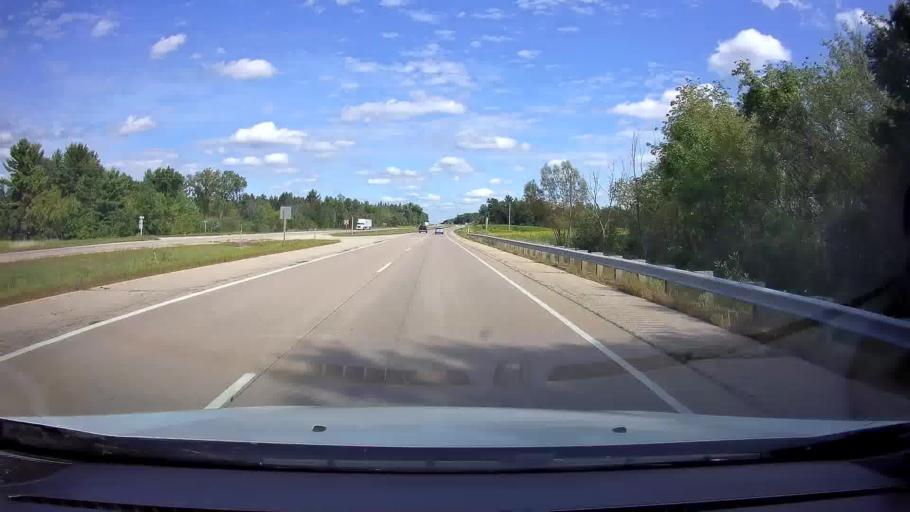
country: US
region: Wisconsin
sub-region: Waupaca County
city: Marion
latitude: 44.8040
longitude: -88.9619
